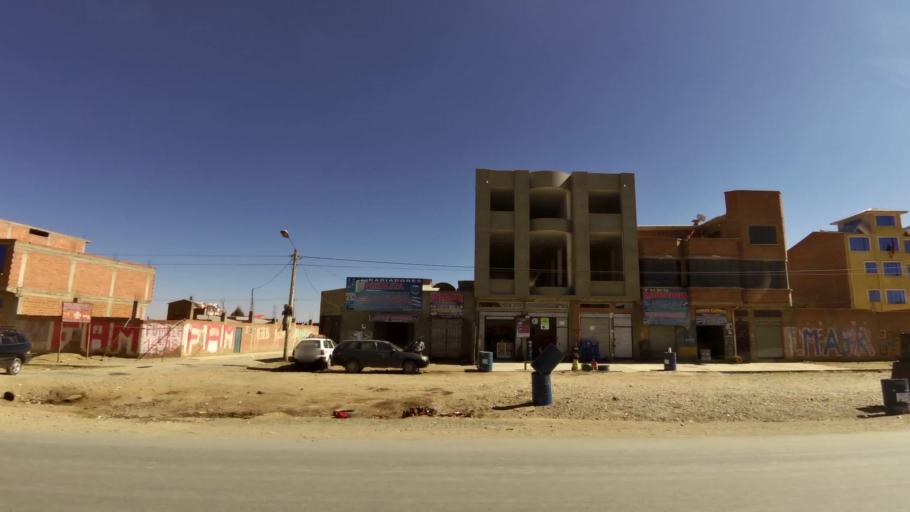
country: BO
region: La Paz
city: La Paz
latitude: -16.5623
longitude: -68.2163
